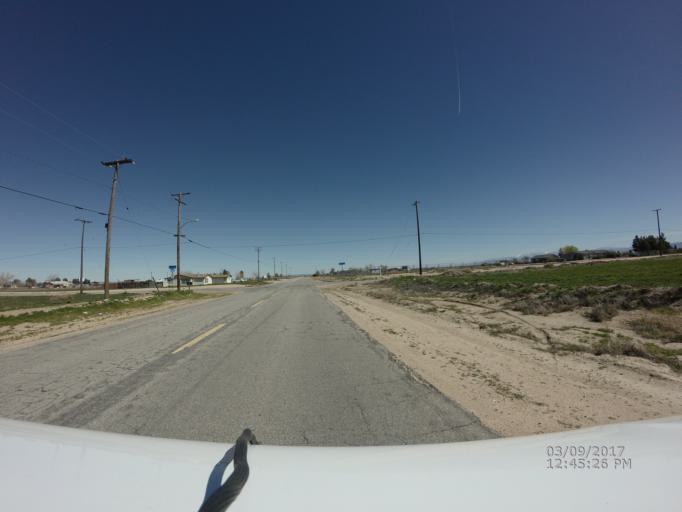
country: US
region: California
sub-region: Los Angeles County
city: Quartz Hill
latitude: 34.7475
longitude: -118.2728
